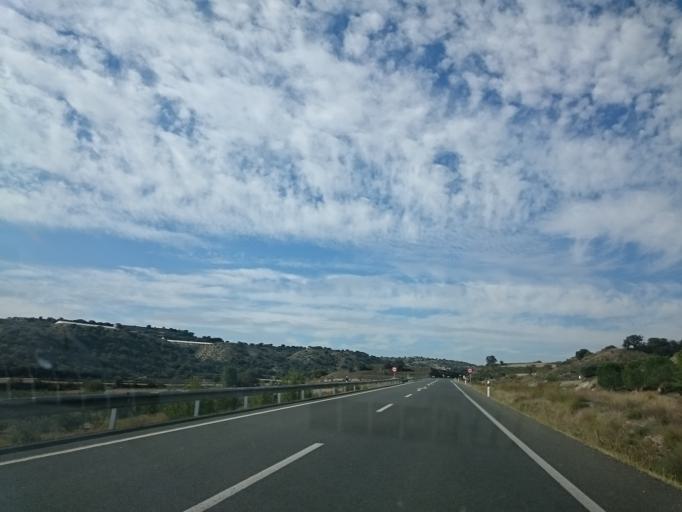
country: ES
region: Aragon
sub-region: Provincia de Huesca
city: Albelda
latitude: 41.8751
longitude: 0.5284
